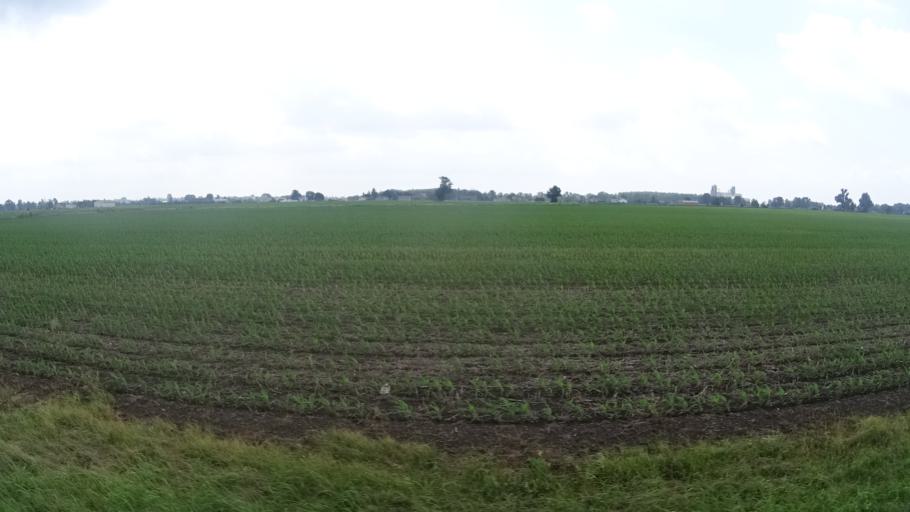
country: US
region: Ohio
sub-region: Huron County
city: Bellevue
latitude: 41.3021
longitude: -82.8099
